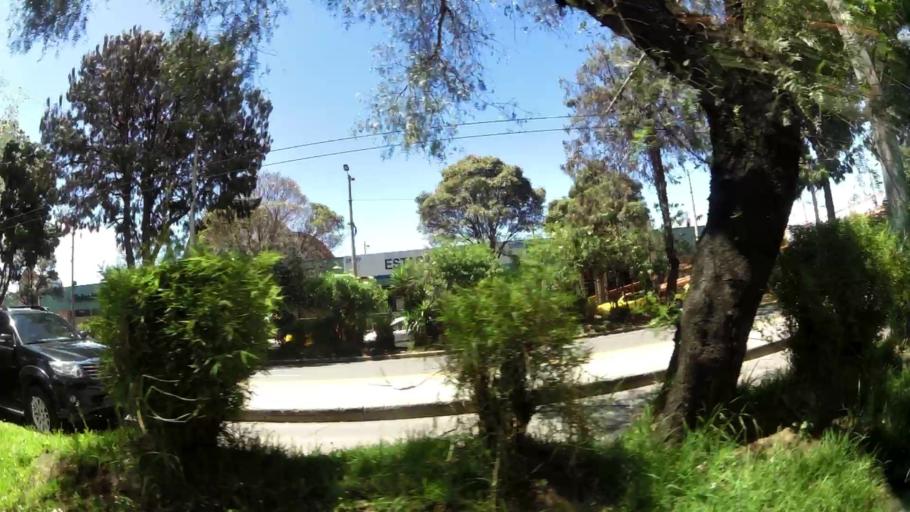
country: EC
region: Pichincha
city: Quito
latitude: -0.1636
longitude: -78.4862
